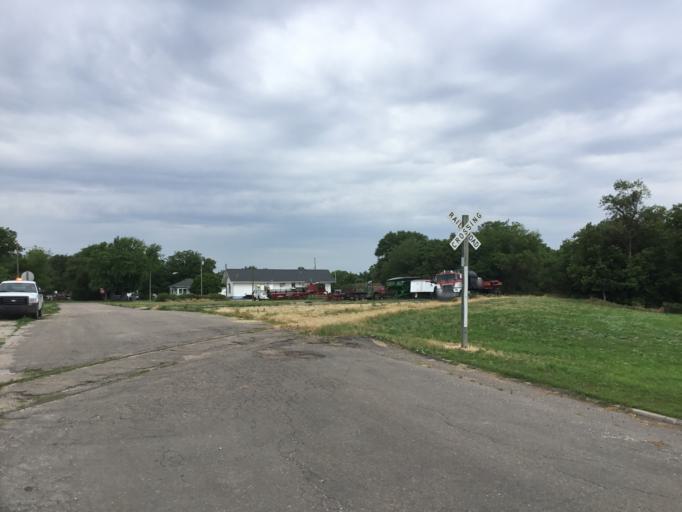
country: US
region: Kansas
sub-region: Republic County
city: Belleville
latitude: 39.8280
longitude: -97.6291
